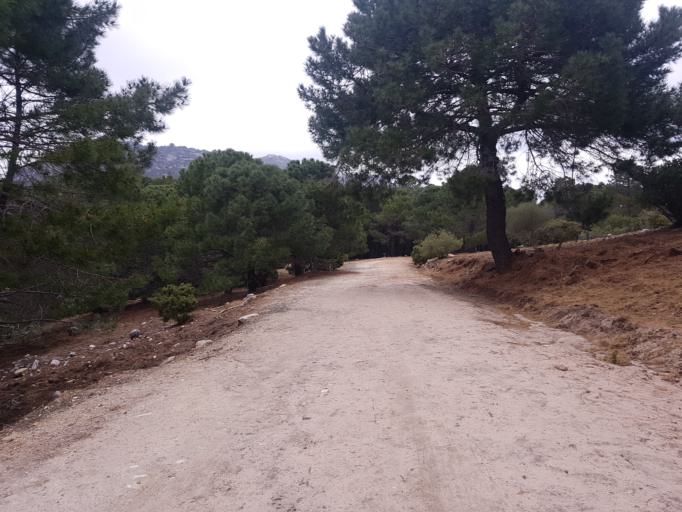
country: ES
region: Andalusia
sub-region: Provincia de Malaga
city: Ojen
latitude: 36.5666
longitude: -4.8912
